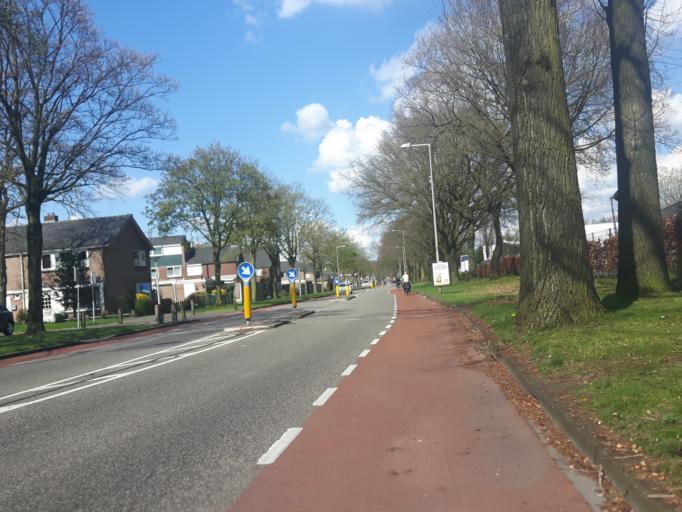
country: NL
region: Overijssel
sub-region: Gemeente Enschede
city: Enschede
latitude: 52.2241
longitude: 6.8681
